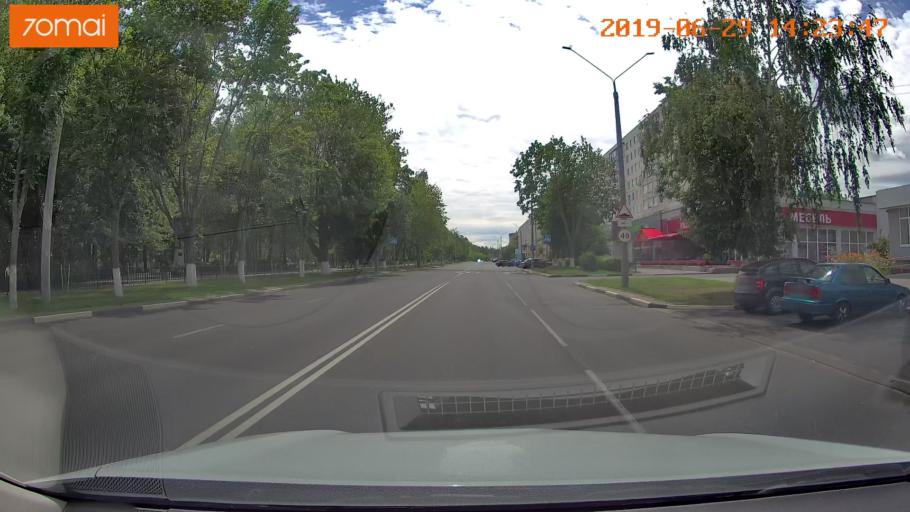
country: BY
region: Minsk
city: Salihorsk
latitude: 52.7836
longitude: 27.5525
